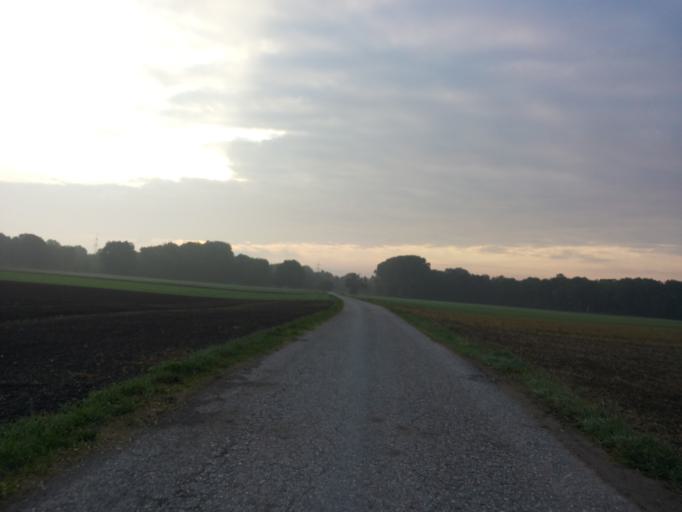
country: DE
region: Bavaria
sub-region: Upper Bavaria
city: Weichering
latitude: 48.7498
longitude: 11.3675
